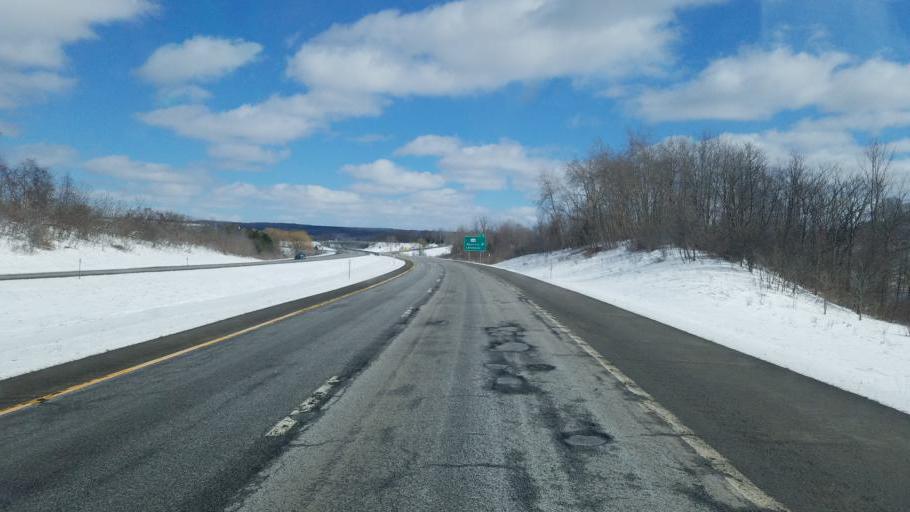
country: US
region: New York
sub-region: Chautauqua County
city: Lakewood
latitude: 42.1519
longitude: -79.4155
